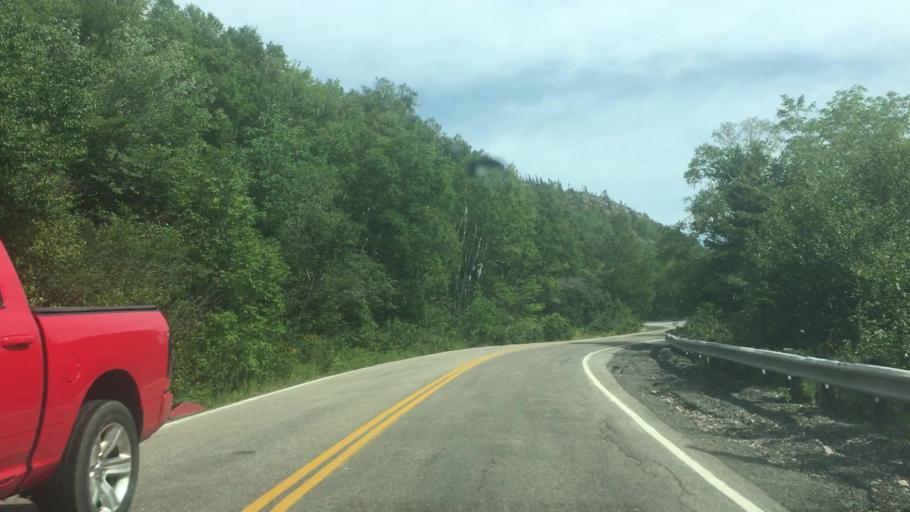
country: CA
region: Nova Scotia
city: Sydney Mines
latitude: 46.5835
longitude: -60.3935
